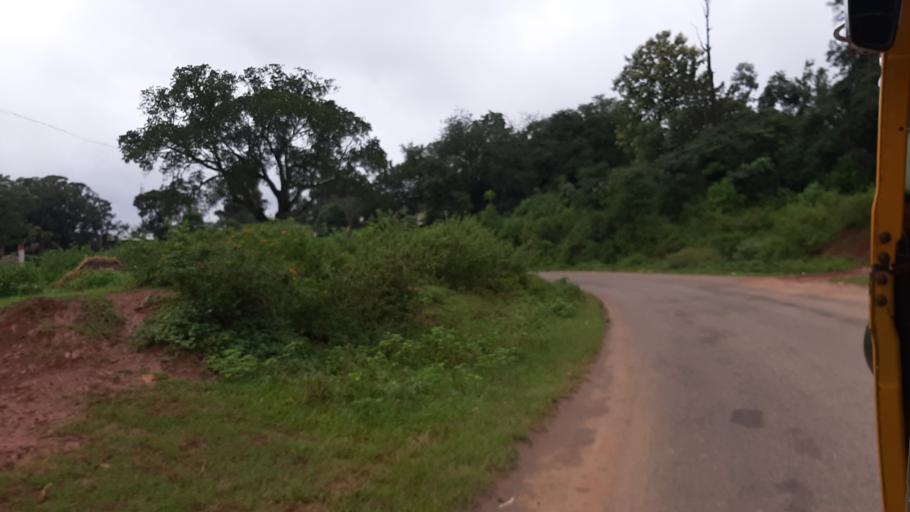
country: IN
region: Andhra Pradesh
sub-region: Vizianagaram District
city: Salur
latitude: 18.3051
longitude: 82.9074
